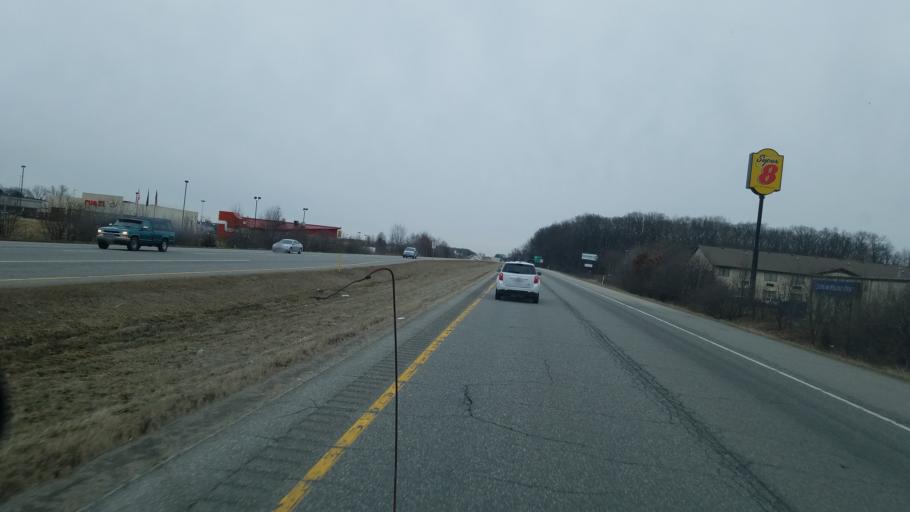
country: US
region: Indiana
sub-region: Marshall County
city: Plymouth
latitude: 41.3615
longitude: -86.3276
